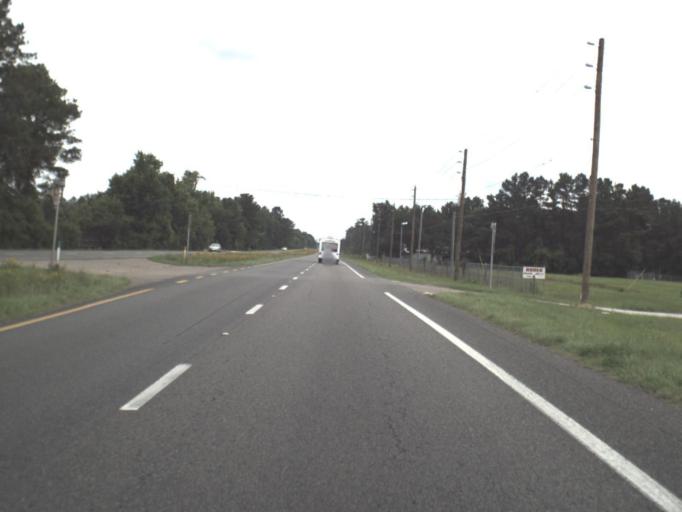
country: US
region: Florida
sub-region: Nassau County
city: Callahan
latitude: 30.5927
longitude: -81.8300
